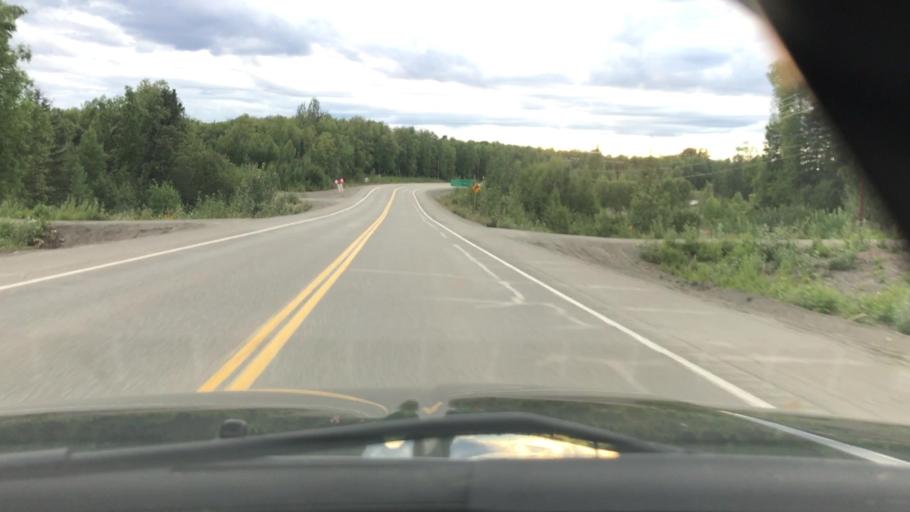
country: US
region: Alaska
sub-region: Matanuska-Susitna Borough
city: Y
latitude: 62.1387
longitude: -150.0503
